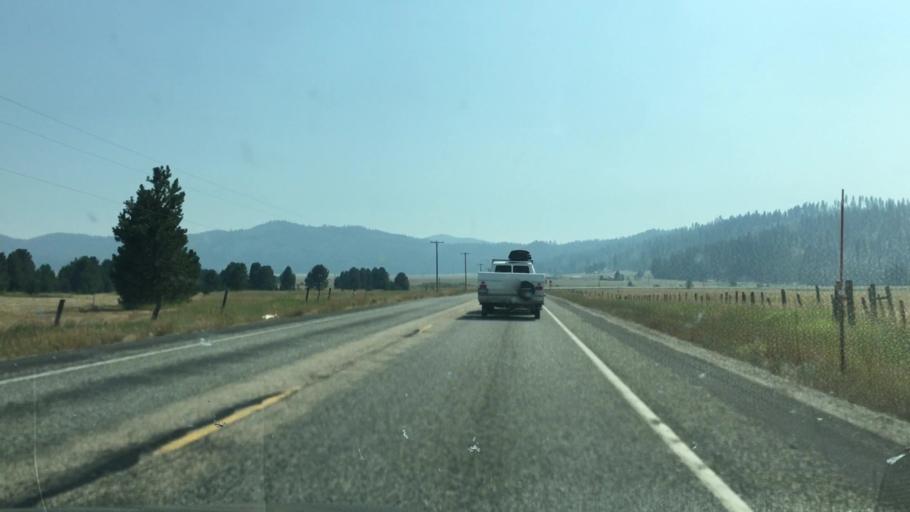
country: US
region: Idaho
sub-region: Valley County
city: Cascade
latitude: 44.3429
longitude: -116.0284
